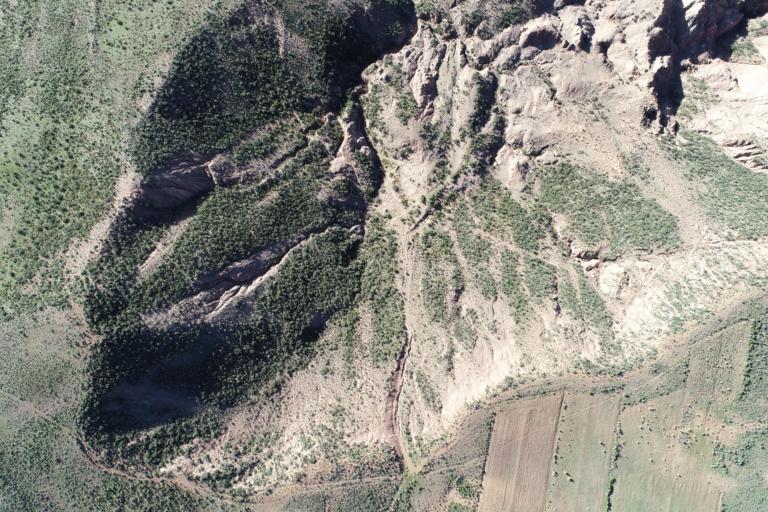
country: BO
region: La Paz
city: Curahuara de Carangas
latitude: -17.3007
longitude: -68.4956
